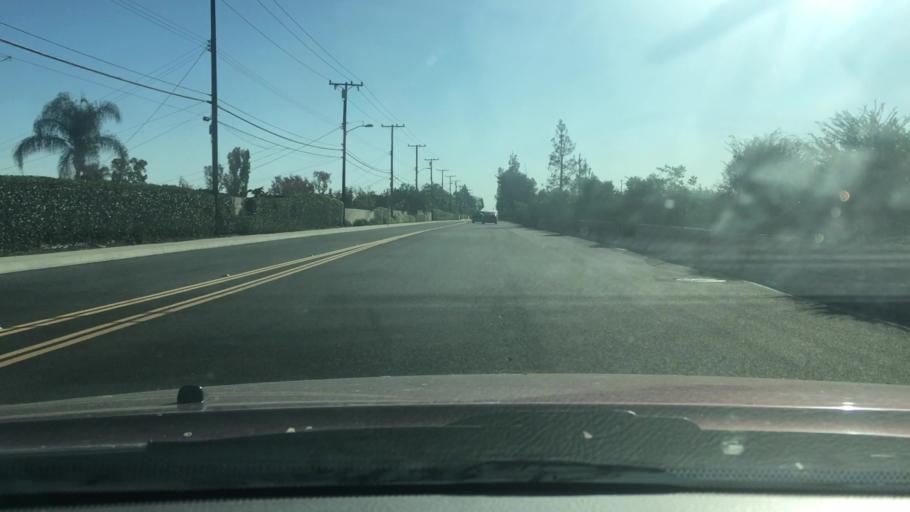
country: US
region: California
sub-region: Los Angeles County
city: La Mirada
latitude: 33.8914
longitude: -118.0177
